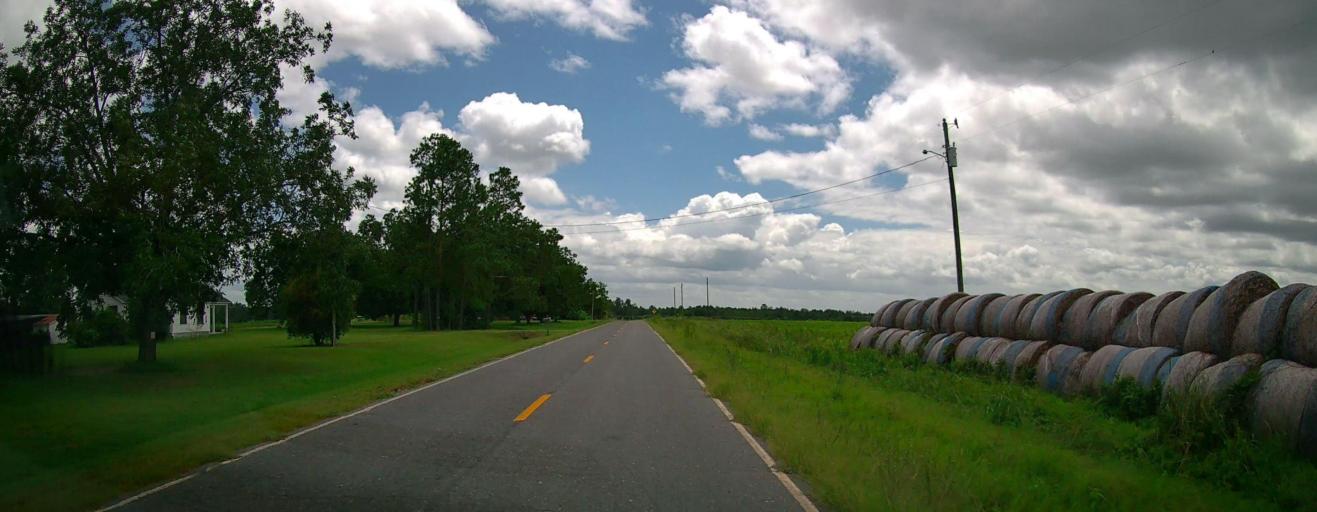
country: US
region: Georgia
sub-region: Ben Hill County
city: Fitzgerald
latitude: 31.6554
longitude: -83.4012
